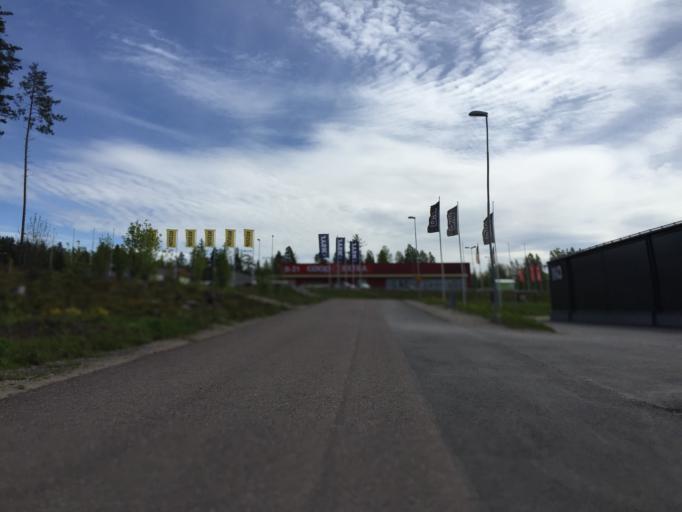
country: SE
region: Dalarna
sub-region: Ludvika Kommun
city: Ludvika
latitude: 60.1360
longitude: 15.1533
